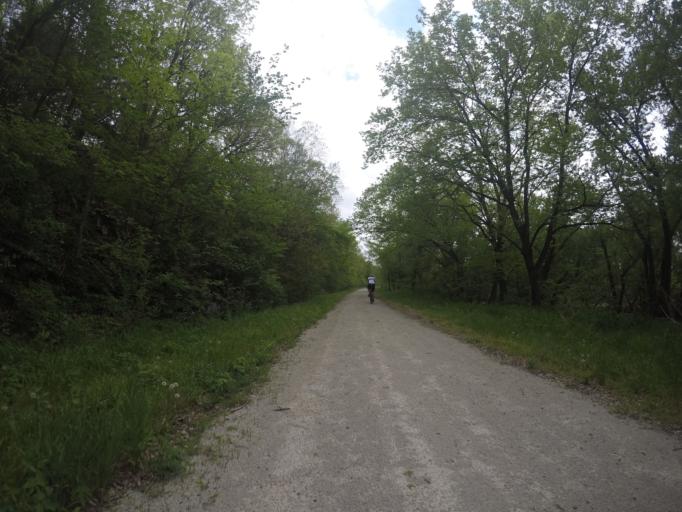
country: US
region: Kansas
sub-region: Marshall County
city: Marysville
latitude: 39.9710
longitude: -96.5999
